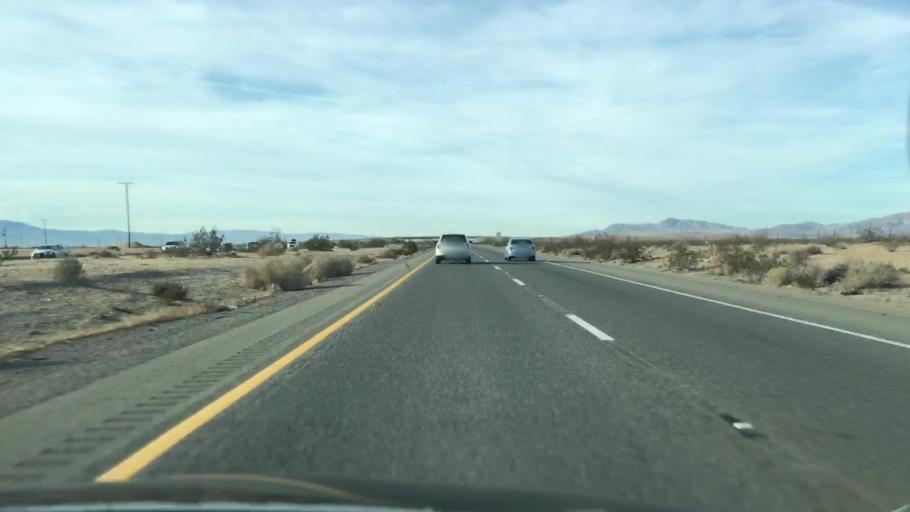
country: US
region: California
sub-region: San Bernardino County
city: Fort Irwin
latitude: 34.9883
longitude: -116.5887
